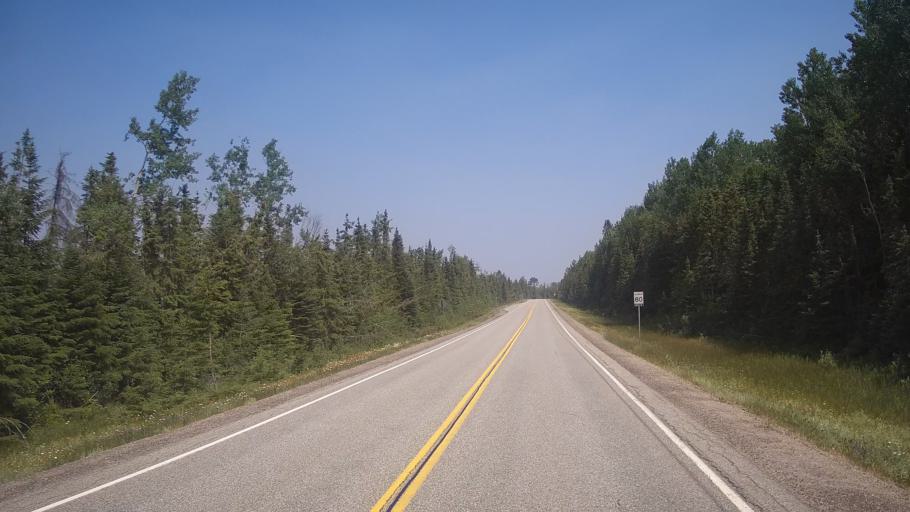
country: CA
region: Ontario
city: Timmins
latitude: 48.0470
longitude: -81.5838
